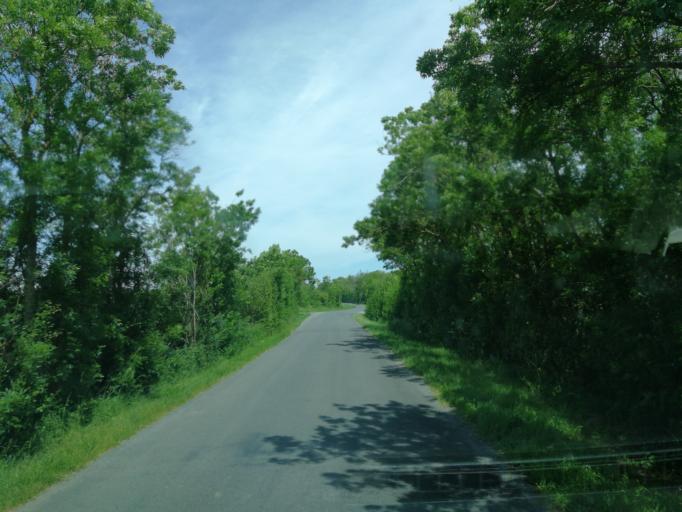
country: FR
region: Pays de la Loire
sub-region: Departement de la Vendee
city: Le Langon
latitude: 46.4031
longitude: -0.9274
